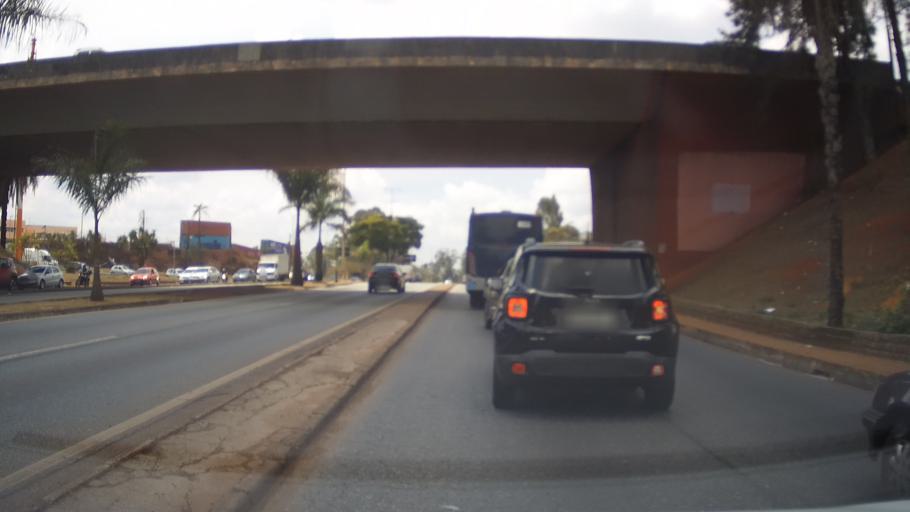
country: BR
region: Minas Gerais
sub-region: Belo Horizonte
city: Belo Horizonte
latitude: -19.9729
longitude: -43.9457
